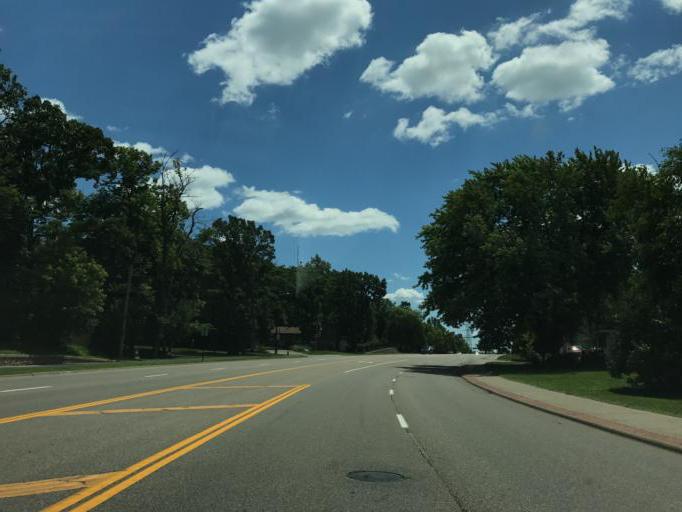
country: US
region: Minnesota
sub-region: Hennepin County
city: Maple Grove
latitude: 45.0721
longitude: -93.4550
